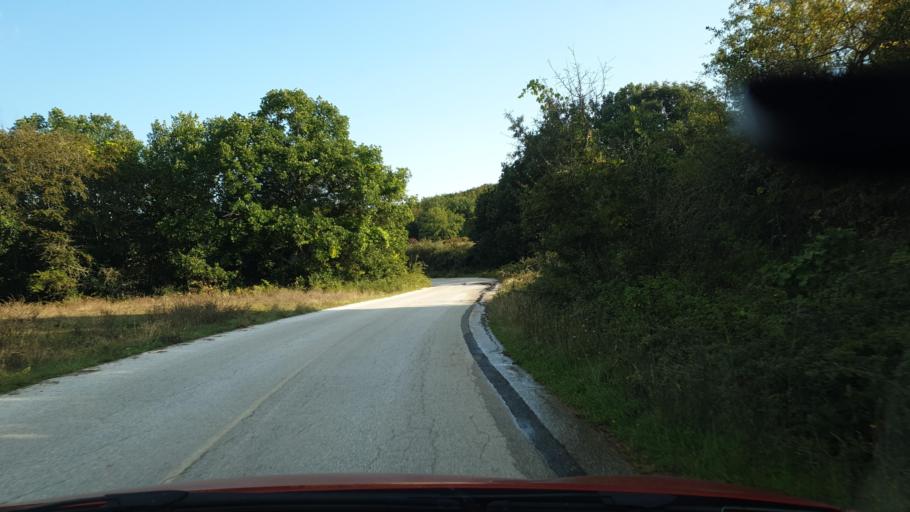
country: GR
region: Central Macedonia
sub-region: Nomos Chalkidikis
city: Galatista
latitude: 40.5074
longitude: 23.2229
